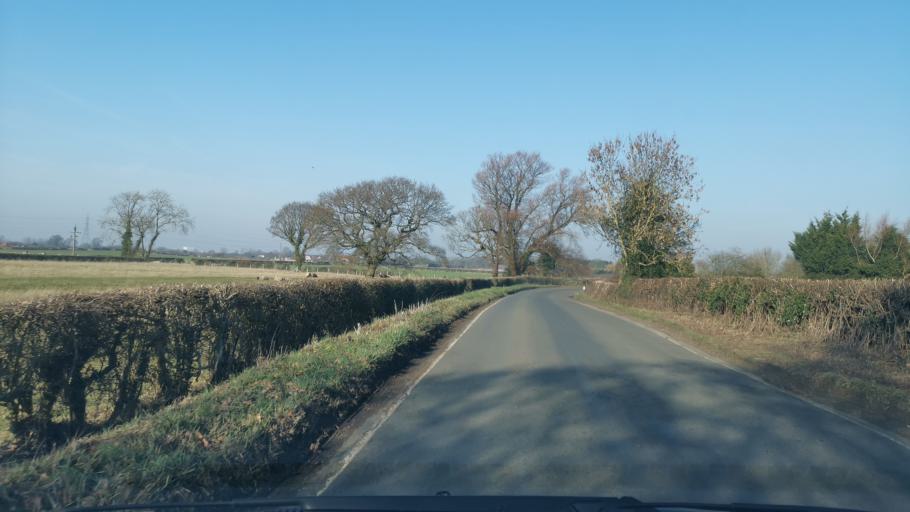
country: GB
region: England
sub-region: City of York
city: Murton
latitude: 53.9708
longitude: -1.0106
